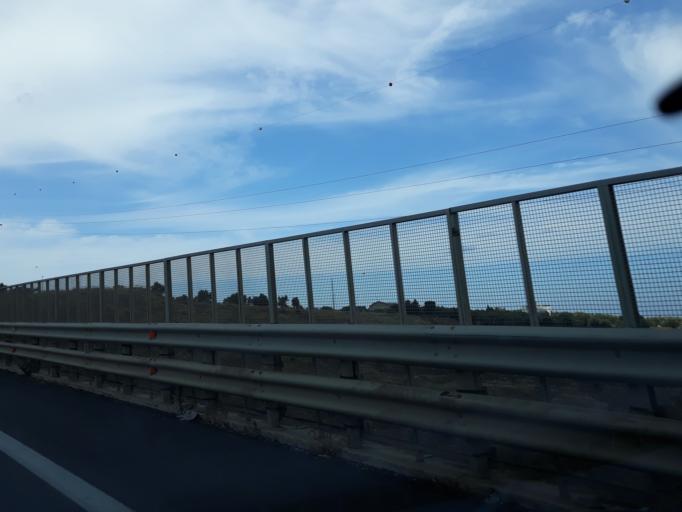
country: IT
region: Sicily
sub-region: Palermo
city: Termini Imerese
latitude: 37.9802
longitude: 13.6710
